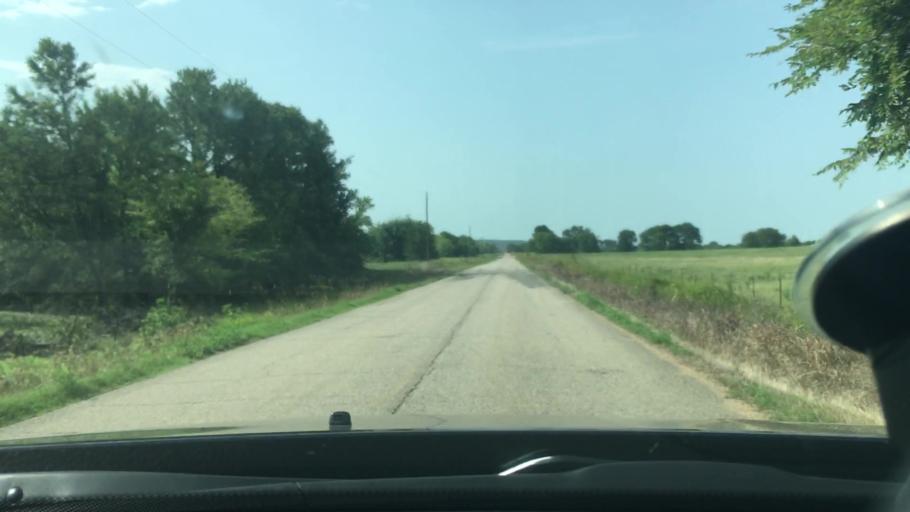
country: US
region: Oklahoma
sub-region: Atoka County
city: Atoka
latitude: 34.4665
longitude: -96.0406
